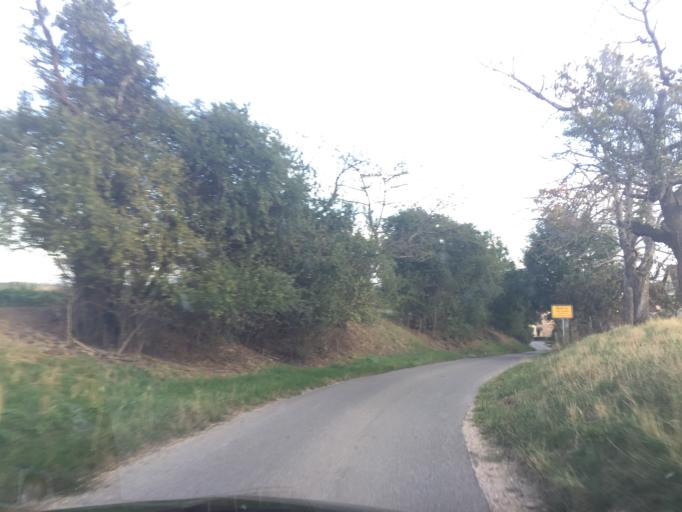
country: DE
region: Thuringia
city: Altkirchen
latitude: 50.9165
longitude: 12.3549
